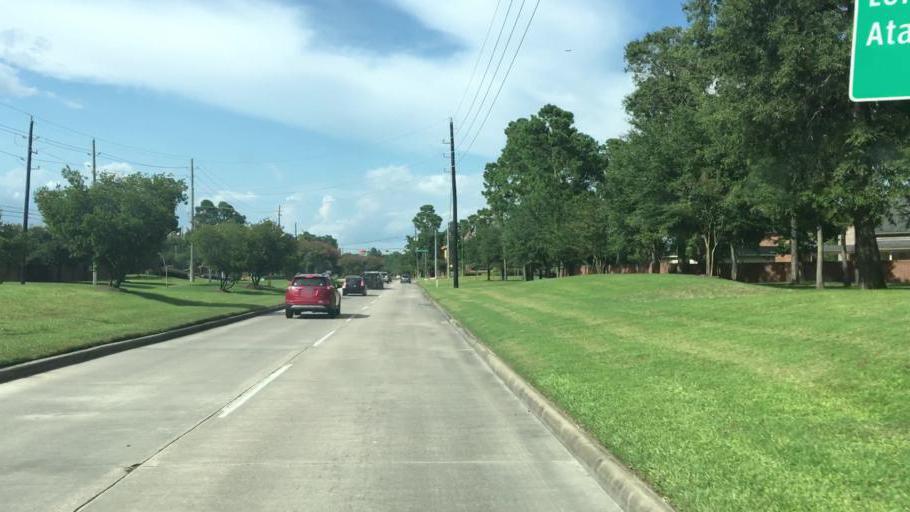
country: US
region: Texas
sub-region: Harris County
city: Atascocita
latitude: 29.9557
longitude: -95.1722
